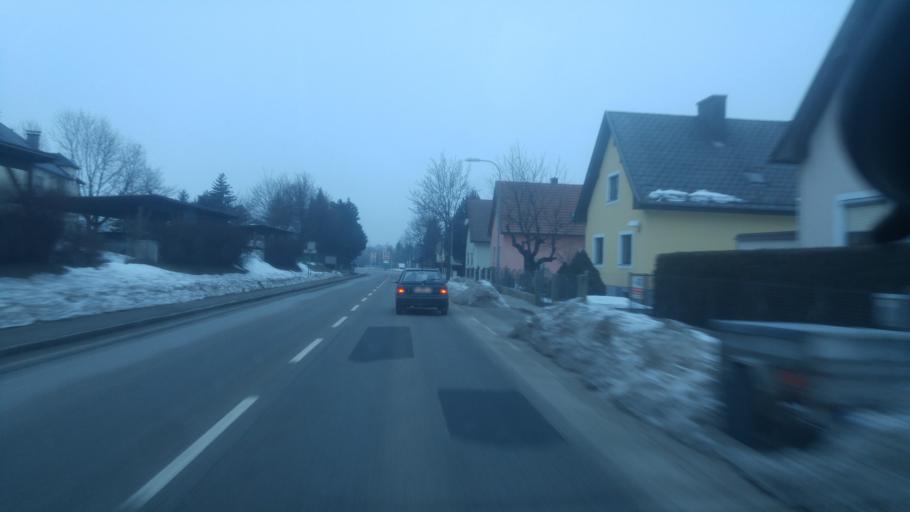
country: AT
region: Lower Austria
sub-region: Politischer Bezirk Lilienfeld
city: Hainfeld
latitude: 48.0385
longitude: 15.7623
